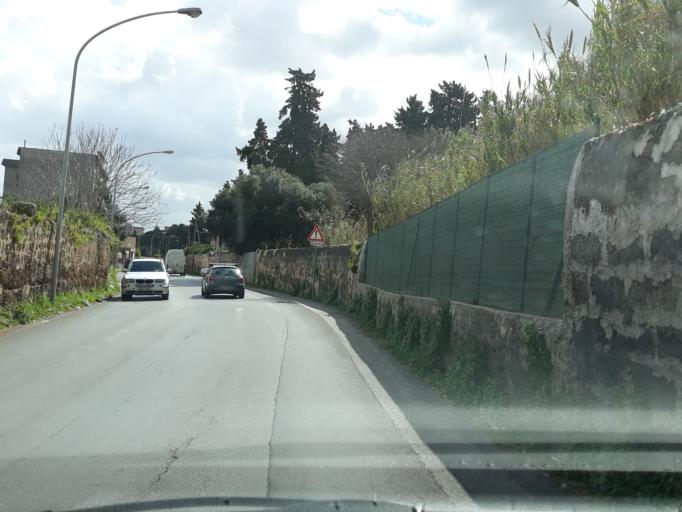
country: IT
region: Sicily
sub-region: Palermo
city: Palermo
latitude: 38.1253
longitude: 13.3152
